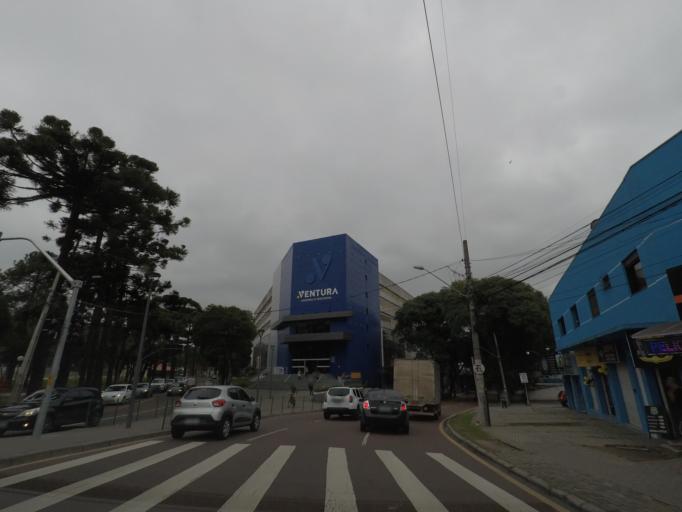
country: BR
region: Parana
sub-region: Curitiba
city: Curitiba
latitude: -25.4778
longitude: -49.2924
